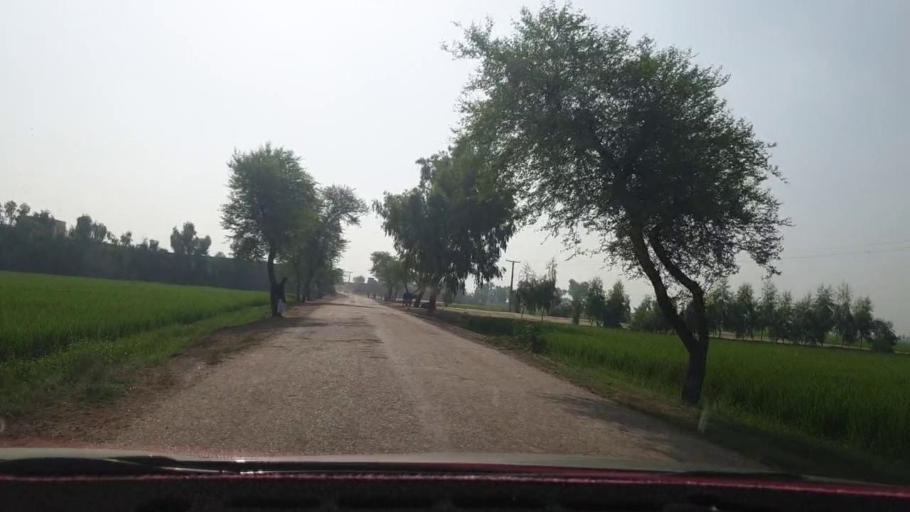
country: PK
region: Sindh
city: Nasirabad
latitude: 27.4399
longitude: 67.9522
